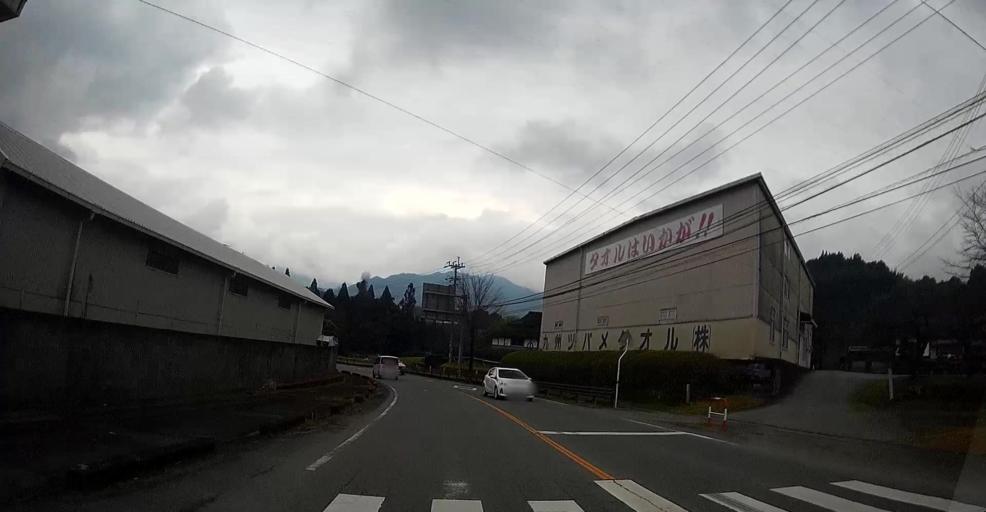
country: JP
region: Kumamoto
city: Matsubase
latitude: 32.6235
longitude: 130.8149
